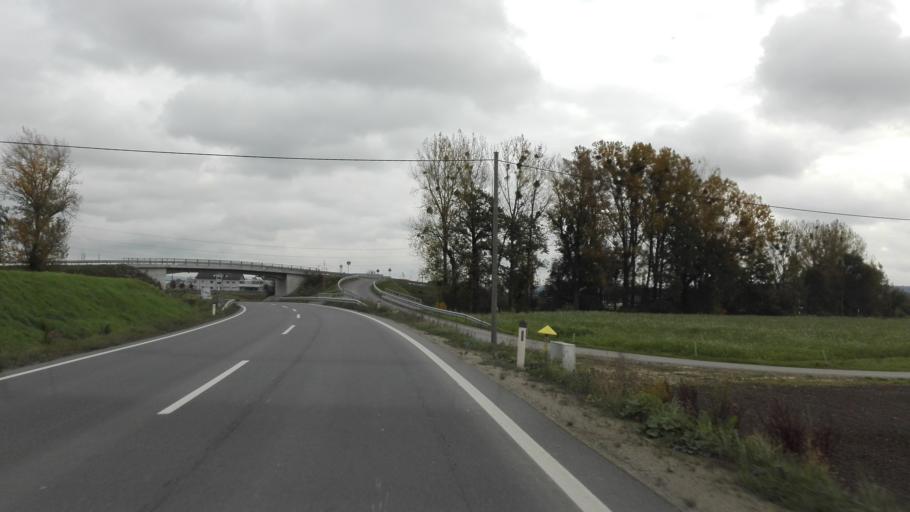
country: AT
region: Upper Austria
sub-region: Politischer Bezirk Urfahr-Umgebung
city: Feldkirchen an der Donau
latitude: 48.2984
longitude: 14.0065
